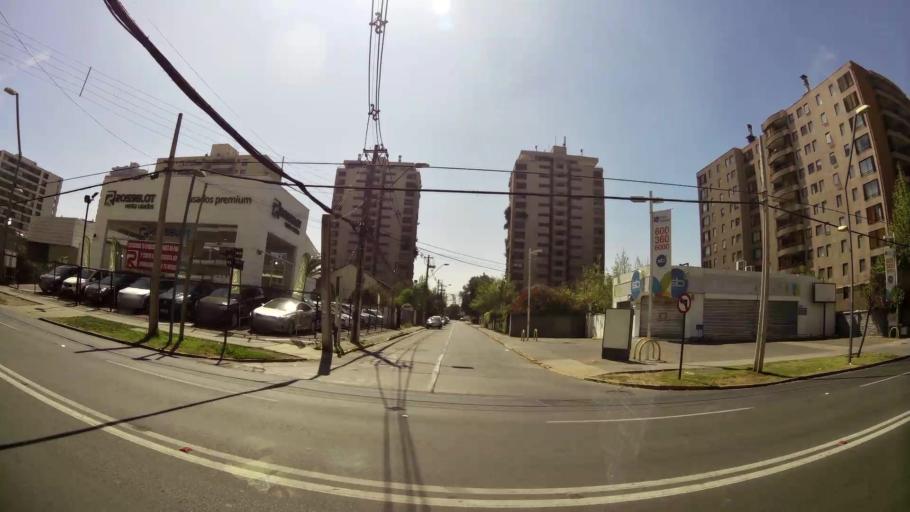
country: CL
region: Santiago Metropolitan
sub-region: Provincia de Santiago
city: Villa Presidente Frei, Nunoa, Santiago, Chile
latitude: -33.4174
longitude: -70.5593
